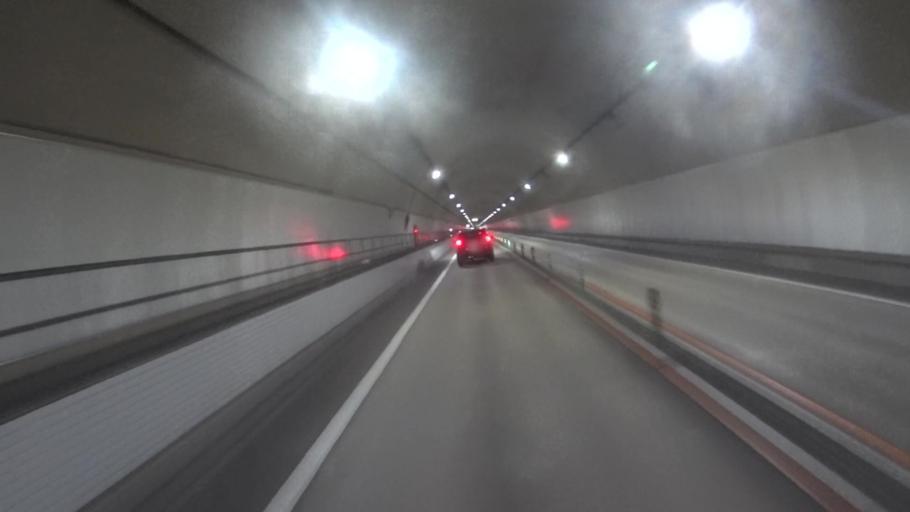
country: JP
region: Kyoto
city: Ayabe
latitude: 35.4037
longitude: 135.2301
